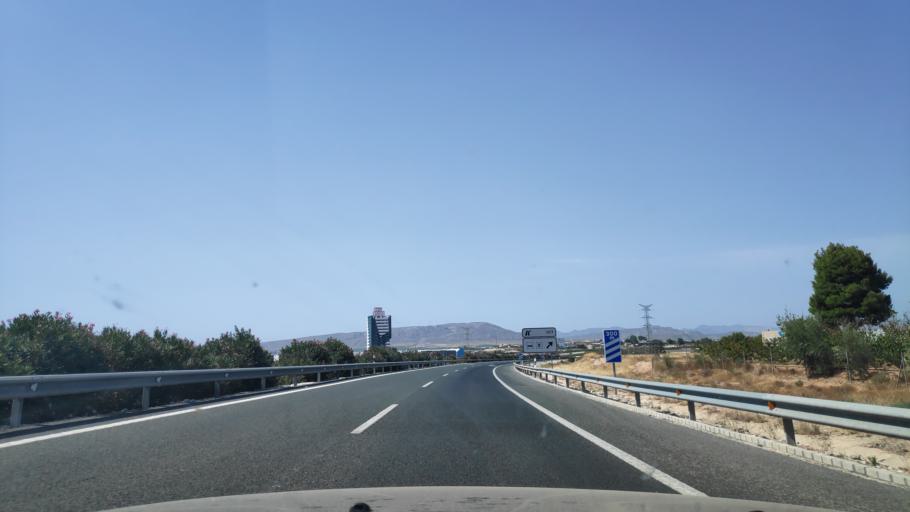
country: ES
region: Murcia
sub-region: Murcia
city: Blanca
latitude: 38.2098
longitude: -1.3511
